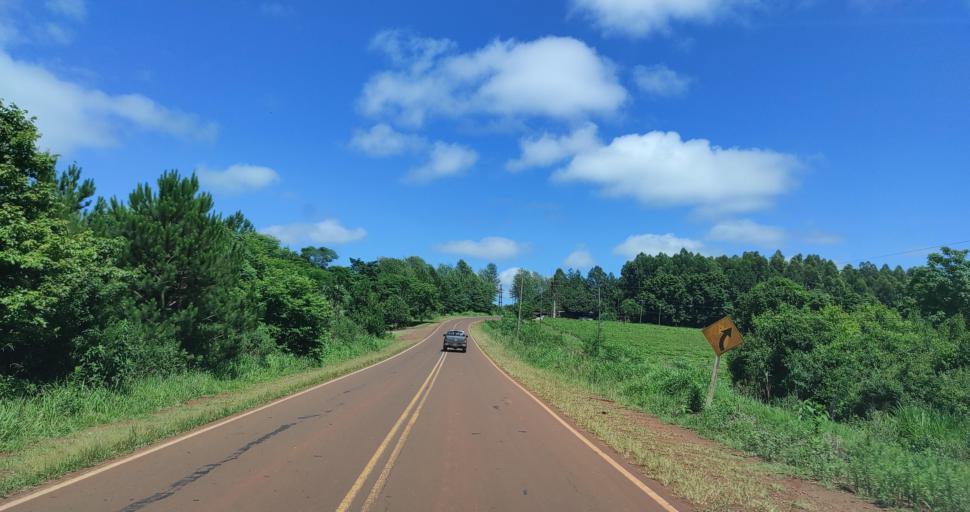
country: AR
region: Misiones
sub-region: Departamento de Veinticinco de Mayo
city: Veinticinco de Mayo
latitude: -27.4114
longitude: -54.7417
